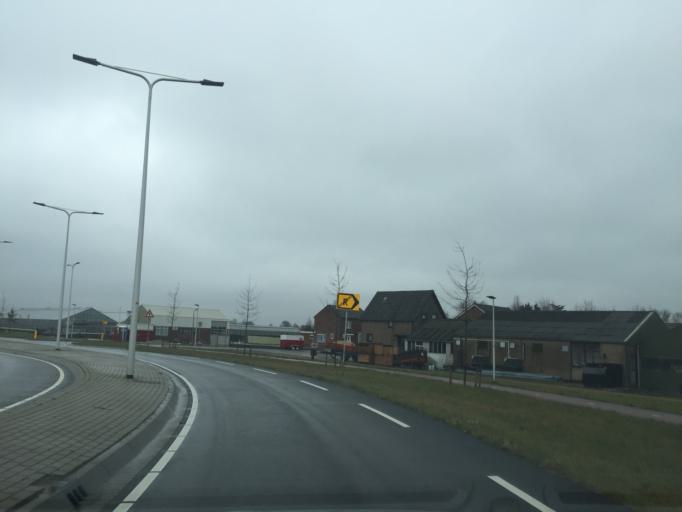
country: NL
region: South Holland
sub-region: Gemeente Kaag en Braassem
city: Oude Wetering
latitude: 52.1995
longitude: 4.6195
